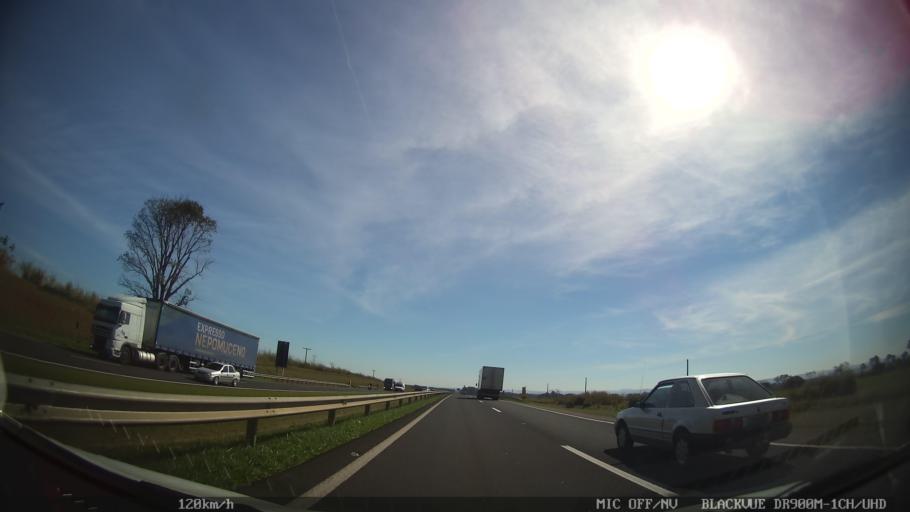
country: BR
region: Sao Paulo
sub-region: Pirassununga
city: Pirassununga
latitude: -21.9781
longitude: -47.4525
